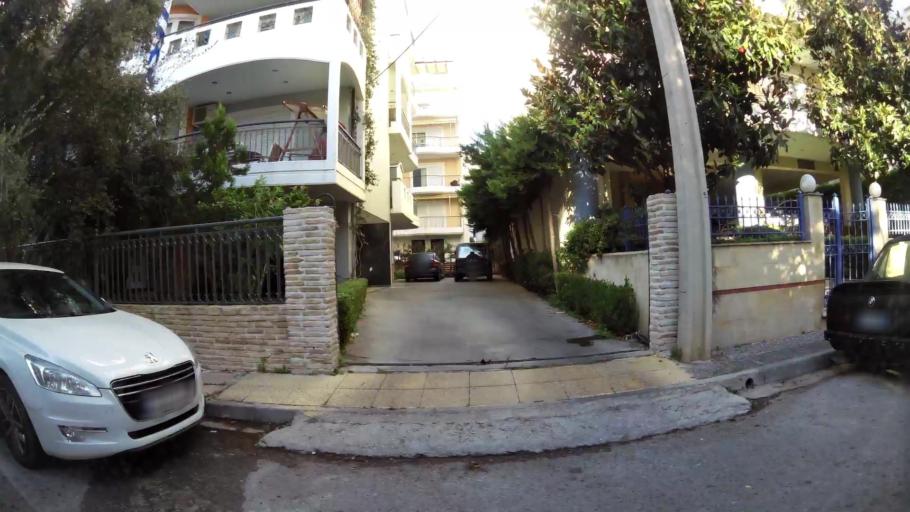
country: GR
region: Attica
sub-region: Nomarchia Anatolikis Attikis
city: Pallini
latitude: 38.0012
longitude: 23.8778
